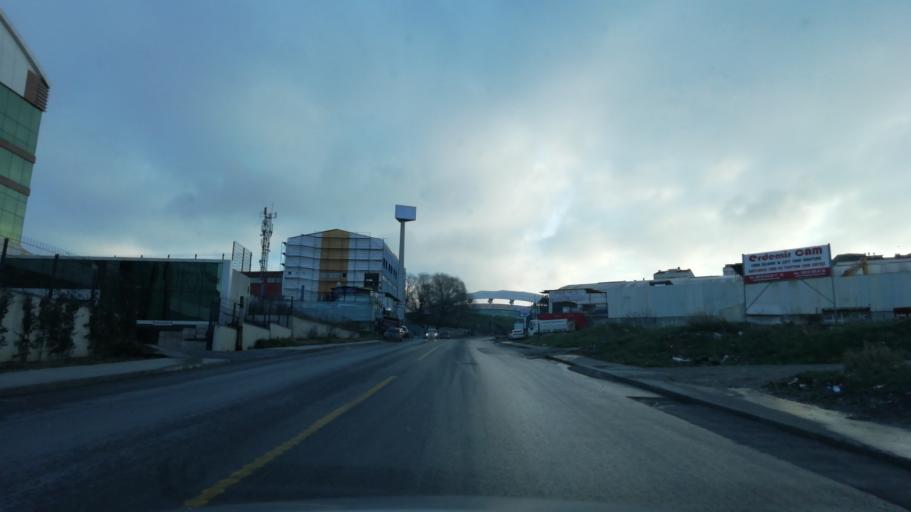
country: TR
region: Istanbul
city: Esenyurt
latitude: 41.0171
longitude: 28.7006
